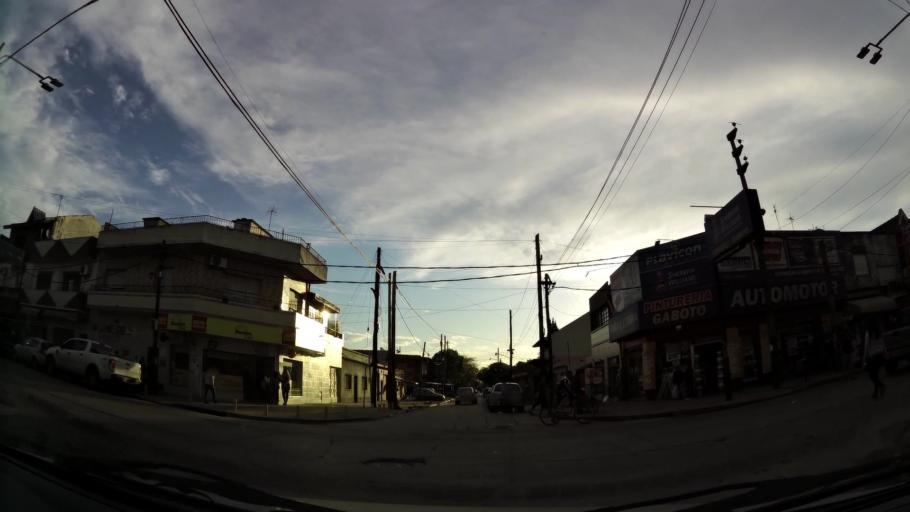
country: AR
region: Buenos Aires
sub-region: Partido de Almirante Brown
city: Adrogue
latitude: -34.7664
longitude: -58.3577
